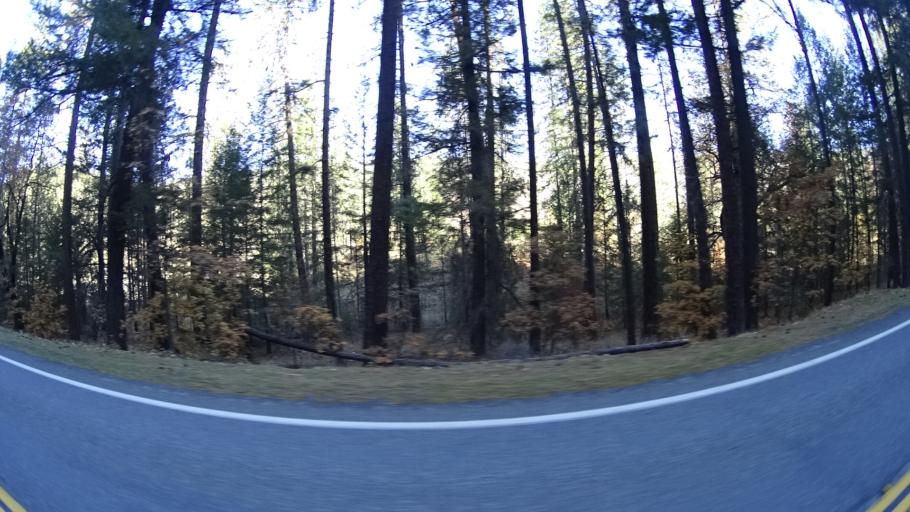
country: US
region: California
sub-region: Siskiyou County
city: Yreka
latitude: 41.8266
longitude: -122.9806
